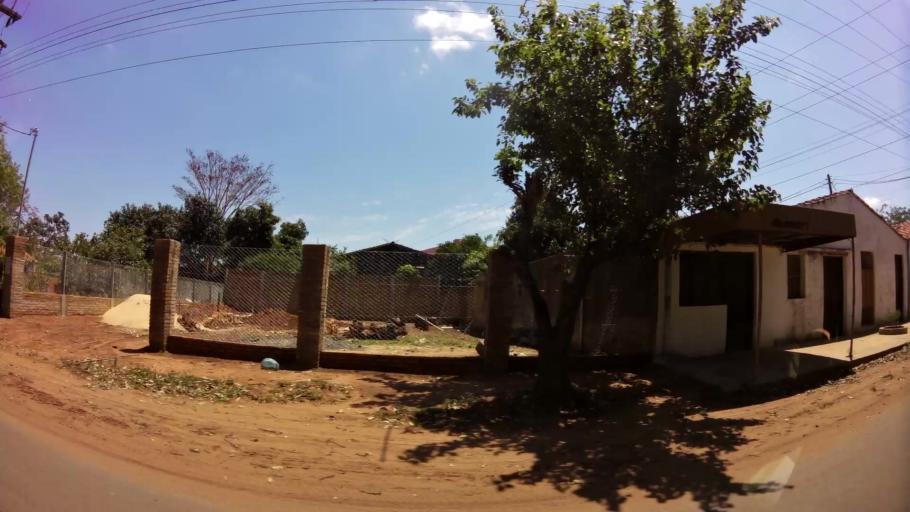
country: PY
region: Central
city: San Antonio
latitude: -25.4263
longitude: -57.5333
